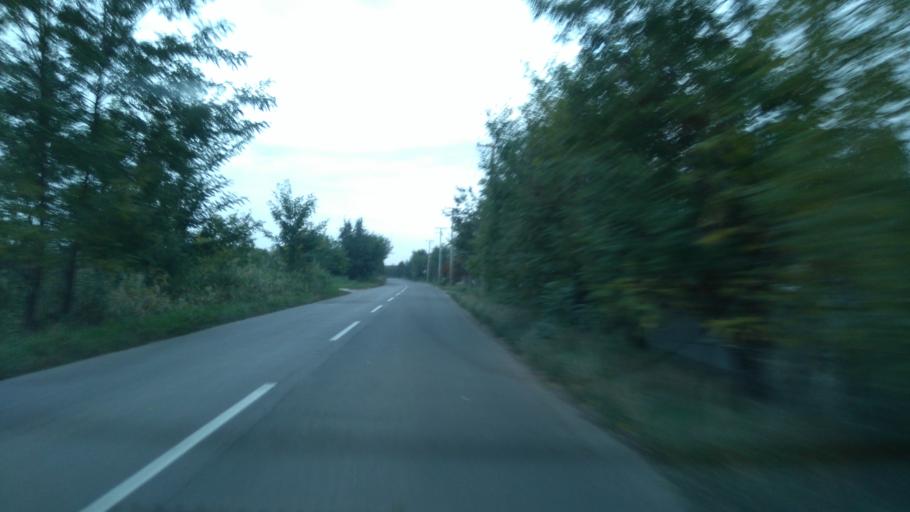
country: RS
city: Mol
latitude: 45.7766
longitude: 20.1346
